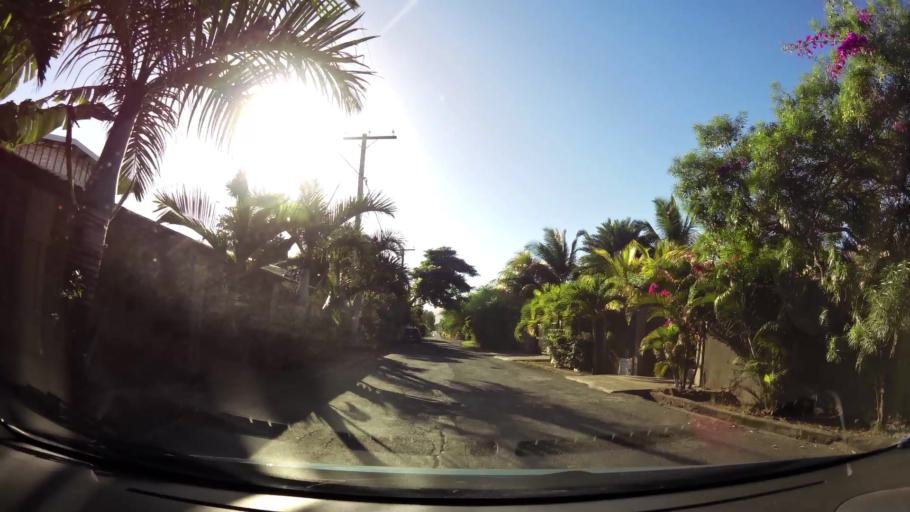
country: MU
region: Black River
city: Tamarin
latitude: -20.3363
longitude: 57.3745
